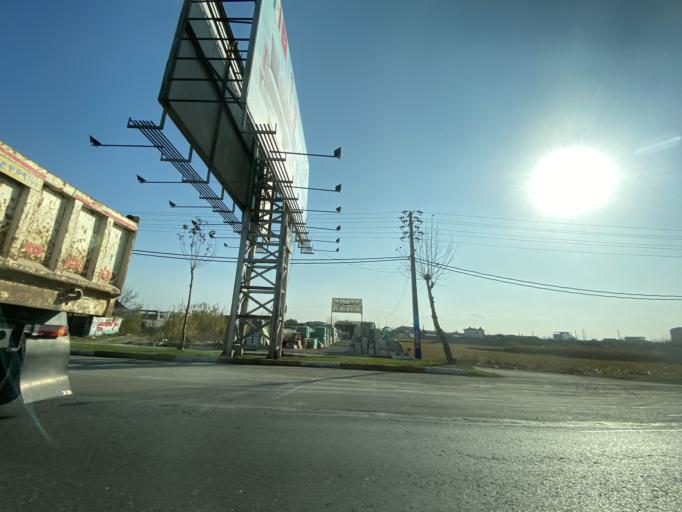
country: IR
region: Mazandaran
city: Babol
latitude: 36.5156
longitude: 52.5714
